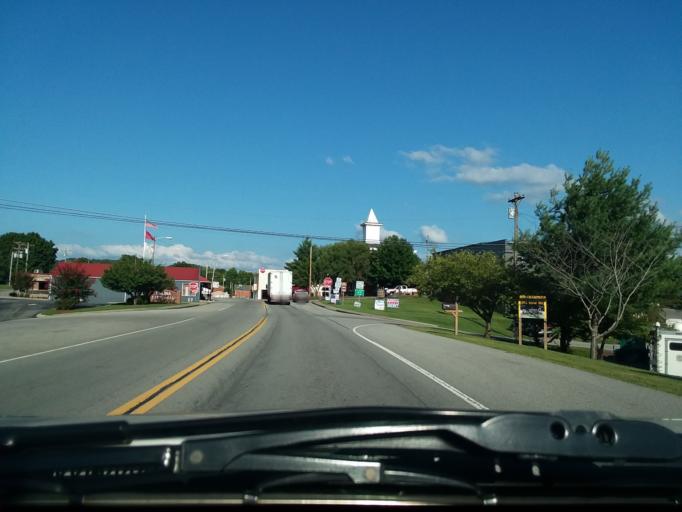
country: US
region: Tennessee
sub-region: Clay County
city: Celina
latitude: 36.5508
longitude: -85.5076
